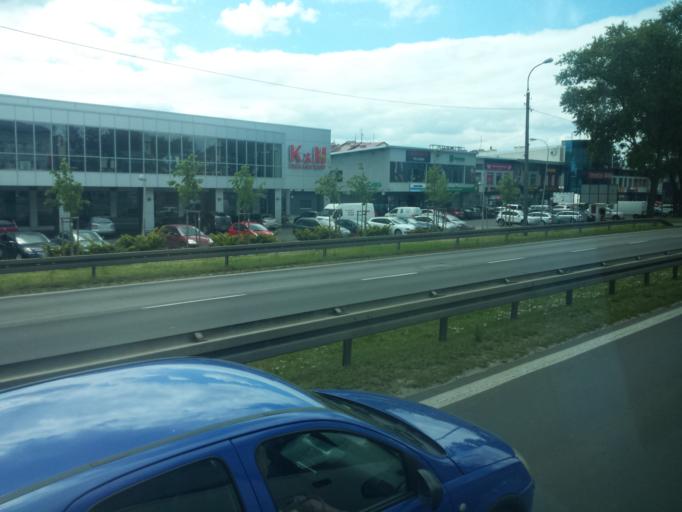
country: PL
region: Masovian Voivodeship
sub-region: Warszawa
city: Wesola
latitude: 52.2234
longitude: 21.2345
